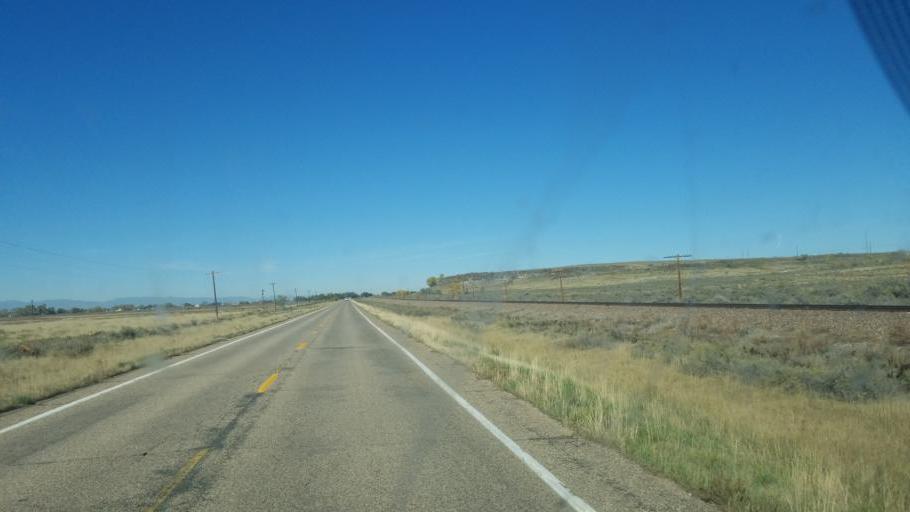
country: US
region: Colorado
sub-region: Pueblo County
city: Pueblo
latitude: 38.2571
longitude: -104.3218
